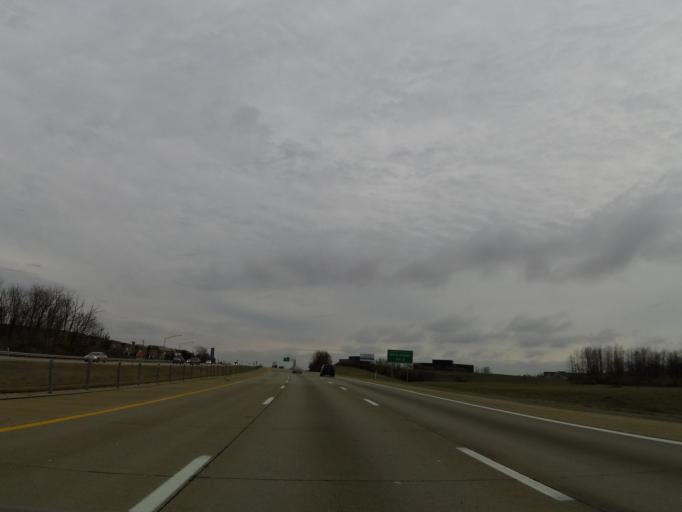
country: US
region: Ohio
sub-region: Hamilton County
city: Delhi Hills
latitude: 39.0574
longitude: -84.6364
